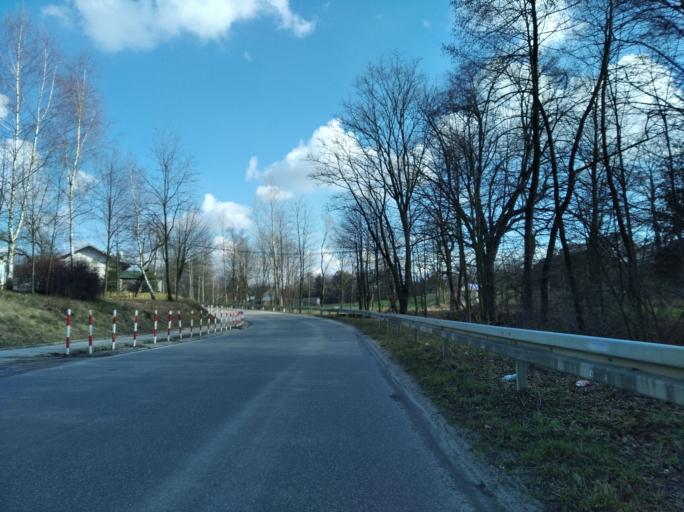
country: PL
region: Subcarpathian Voivodeship
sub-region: Powiat jasielski
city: Kolaczyce
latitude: 49.8522
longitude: 21.5061
